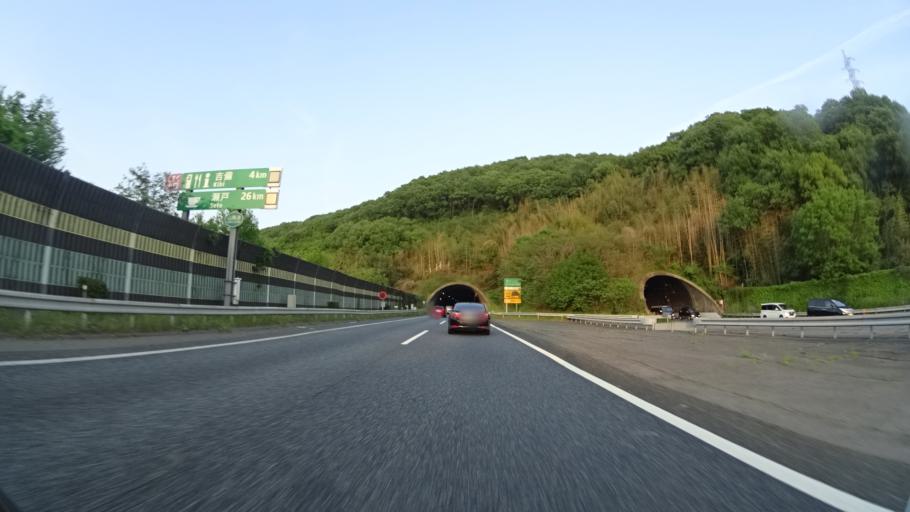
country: JP
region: Okayama
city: Soja
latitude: 34.6806
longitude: 133.8335
